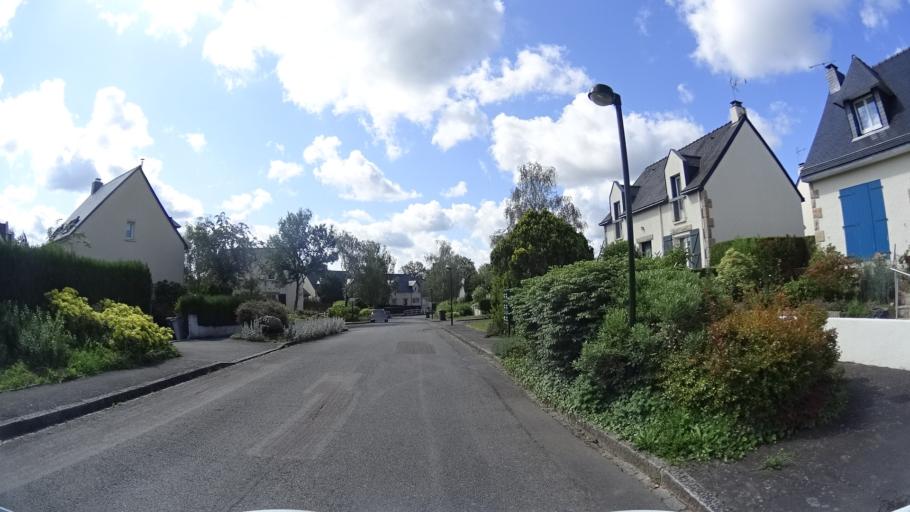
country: FR
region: Brittany
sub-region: Departement d'Ille-et-Vilaine
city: Chartres-de-Bretagne
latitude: 48.0402
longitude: -1.6941
